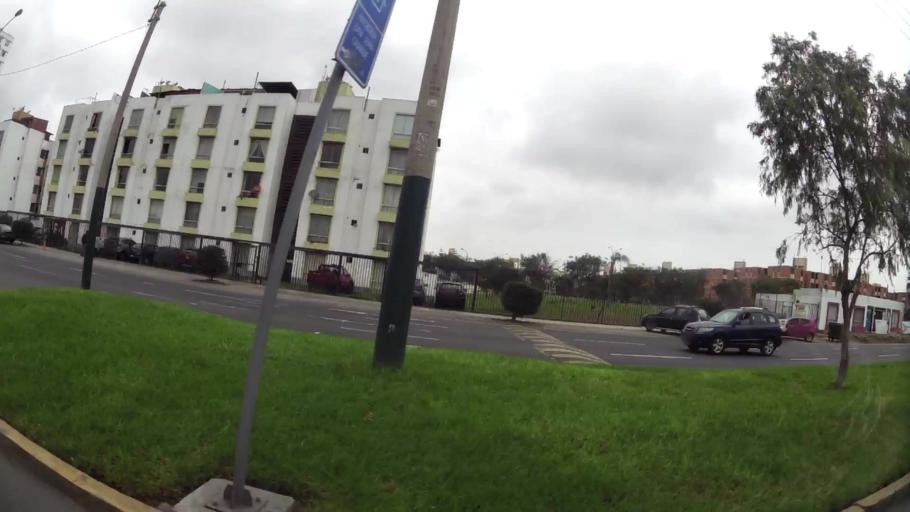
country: PE
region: Lima
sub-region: Lima
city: Surco
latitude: -12.1567
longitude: -76.9899
